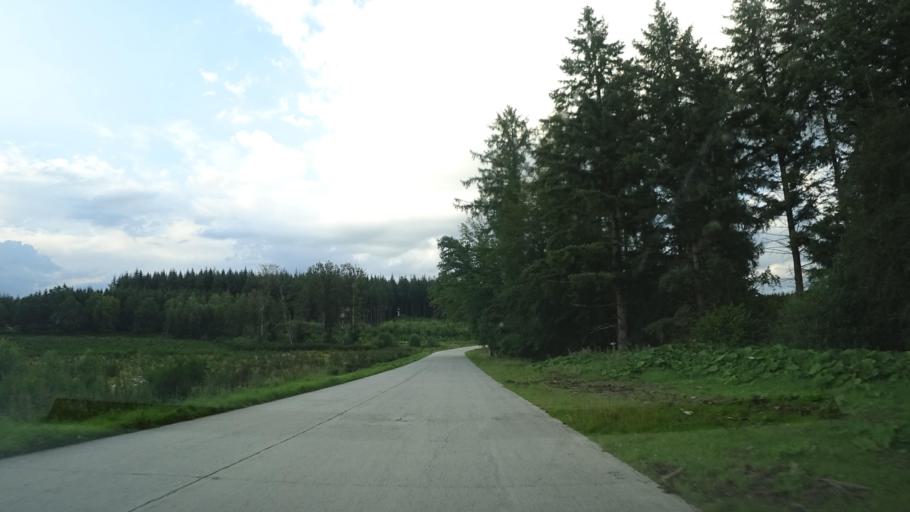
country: BE
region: Wallonia
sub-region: Province du Luxembourg
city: Herbeumont
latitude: 49.7900
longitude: 5.2534
